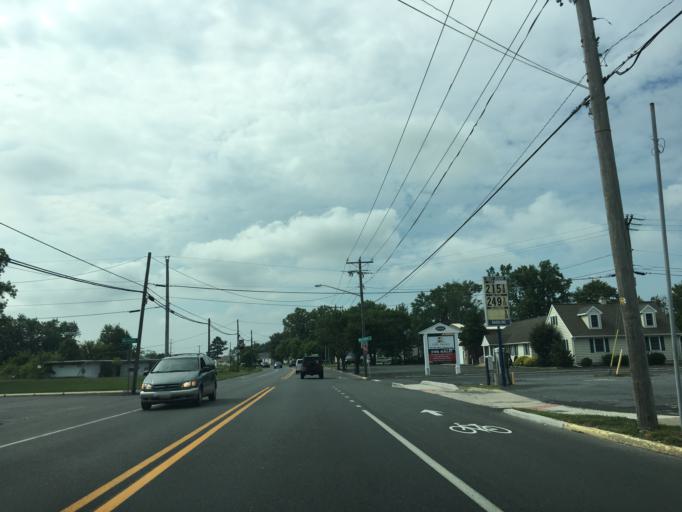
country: US
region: Delaware
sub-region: Sussex County
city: Millsboro
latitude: 38.5524
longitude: -75.2481
